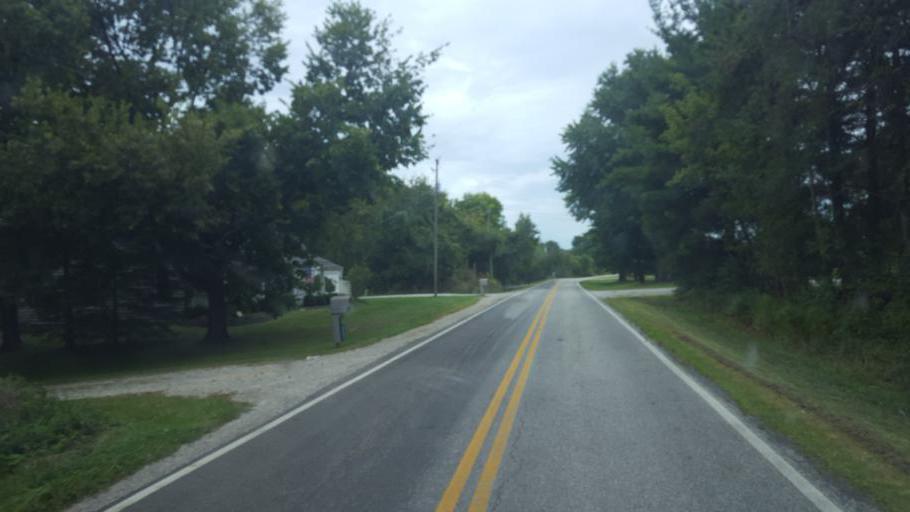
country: US
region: Ohio
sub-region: Delaware County
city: Sunbury
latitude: 40.2637
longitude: -82.8058
